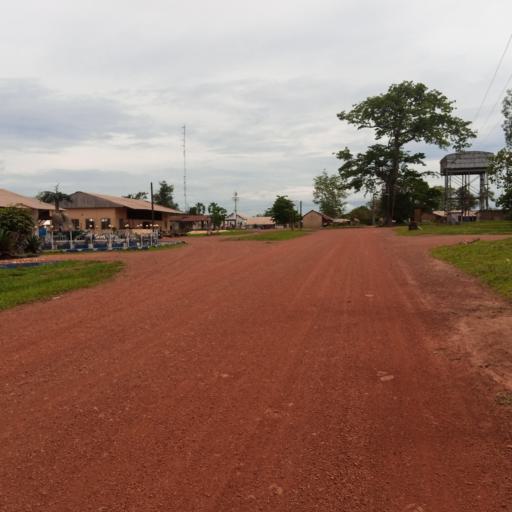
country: SL
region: Southern Province
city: Largo
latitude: 8.1108
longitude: -12.0776
